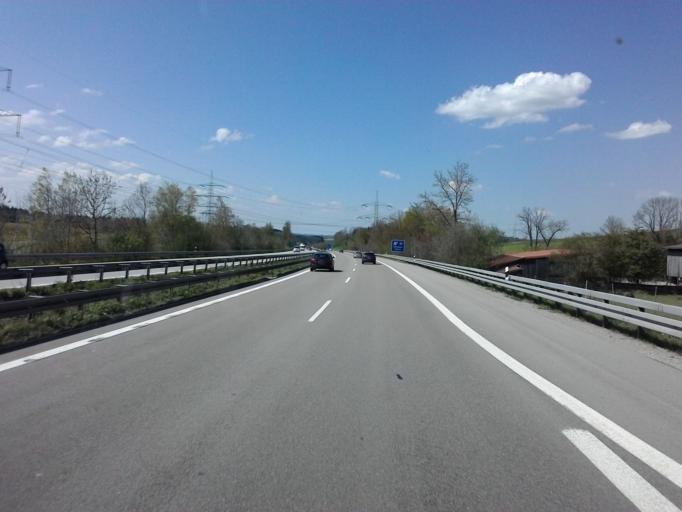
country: DE
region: Bavaria
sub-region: Swabia
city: Durach
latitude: 47.7062
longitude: 10.3664
